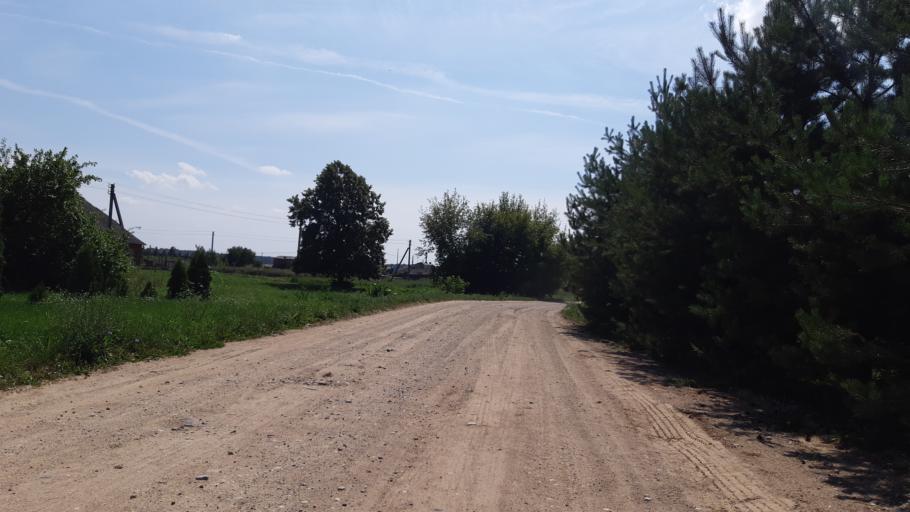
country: LT
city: Virbalis
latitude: 54.6235
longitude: 22.8099
